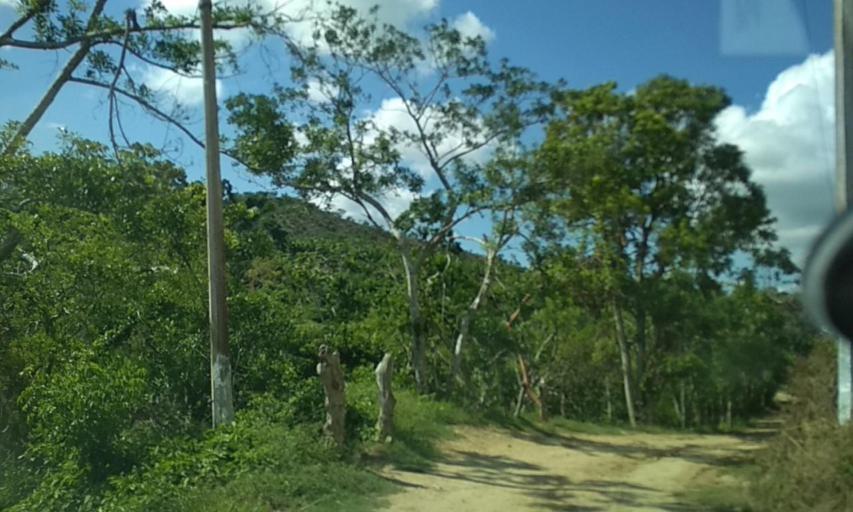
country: MX
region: Veracruz
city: Cazones de Herrera
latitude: 20.6228
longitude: -97.3318
